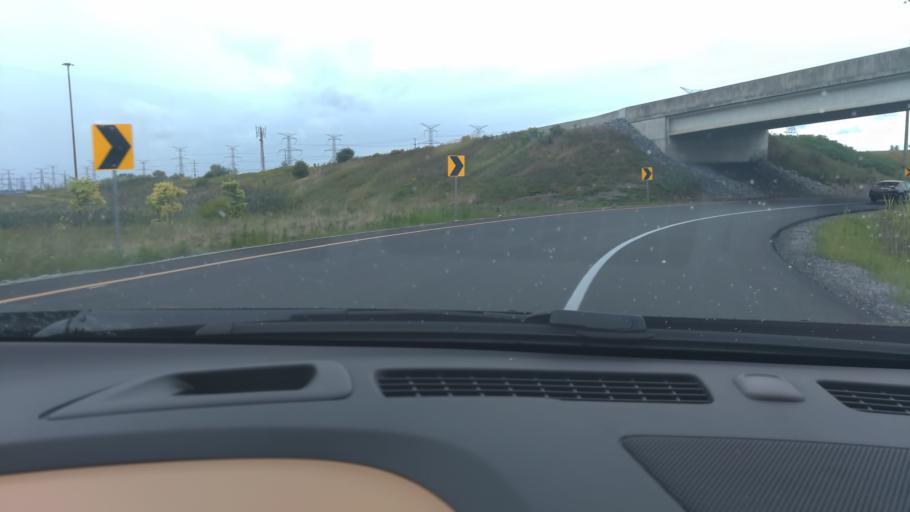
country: CA
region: Ontario
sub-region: York
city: Richmond Hill
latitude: 43.8388
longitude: -79.3653
